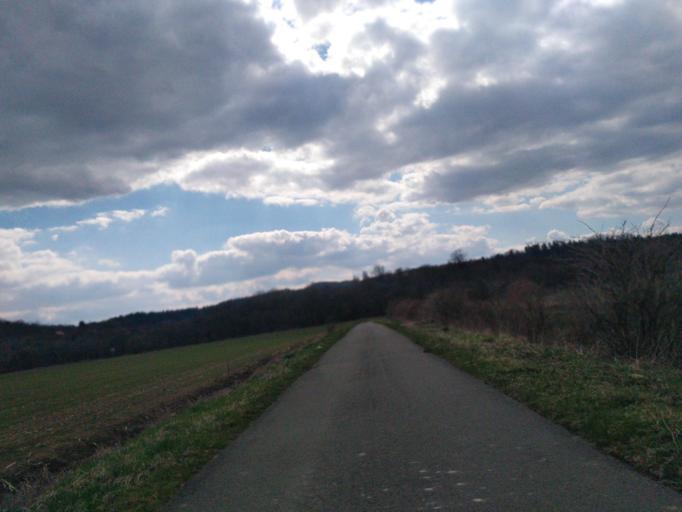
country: PL
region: Subcarpathian Voivodeship
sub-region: Powiat brzozowski
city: Dydnia
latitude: 49.6699
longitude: 22.2624
